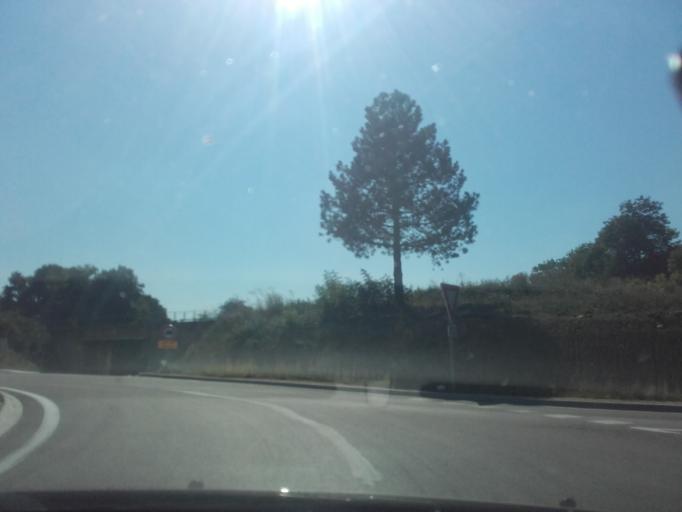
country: FR
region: Bourgogne
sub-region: Departement de la Cote-d'Or
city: Nolay
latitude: 46.9482
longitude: 4.6718
